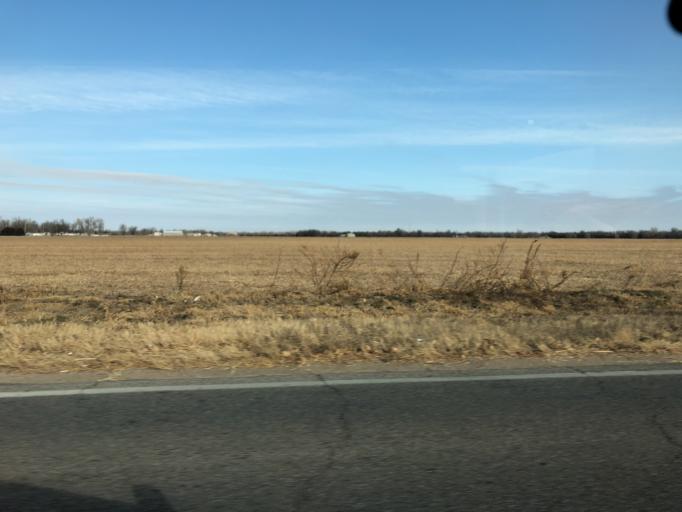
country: US
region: Kansas
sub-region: Reno County
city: South Hutchinson
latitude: 38.0572
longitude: -97.9756
